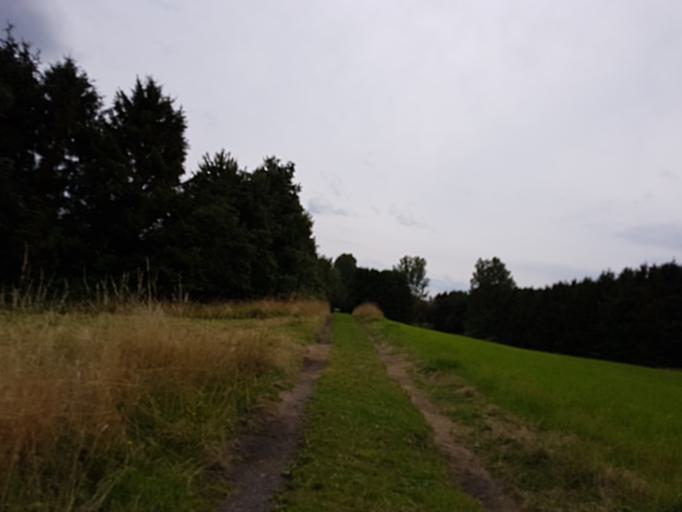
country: DK
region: Capital Region
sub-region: Egedal Kommune
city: Stenlose
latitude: 55.7940
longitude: 12.1970
